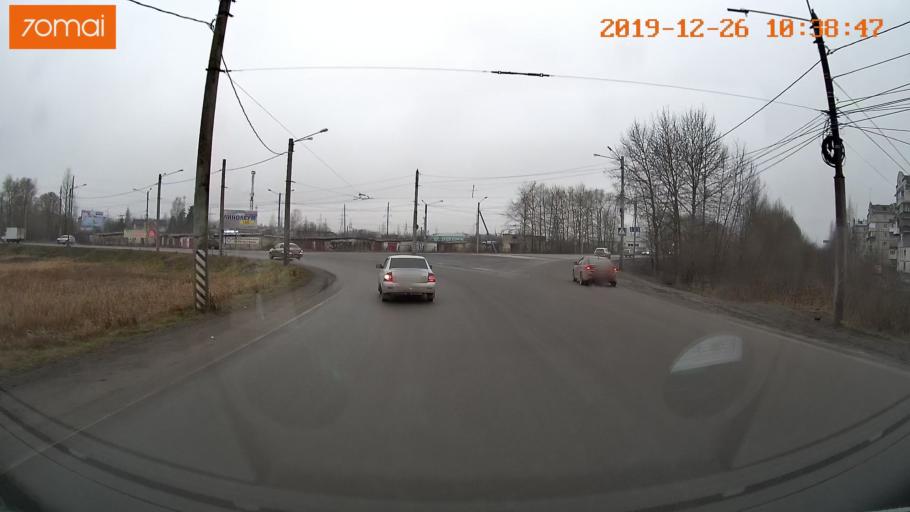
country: RU
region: Vologda
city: Vologda
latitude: 59.1875
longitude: 39.8518
